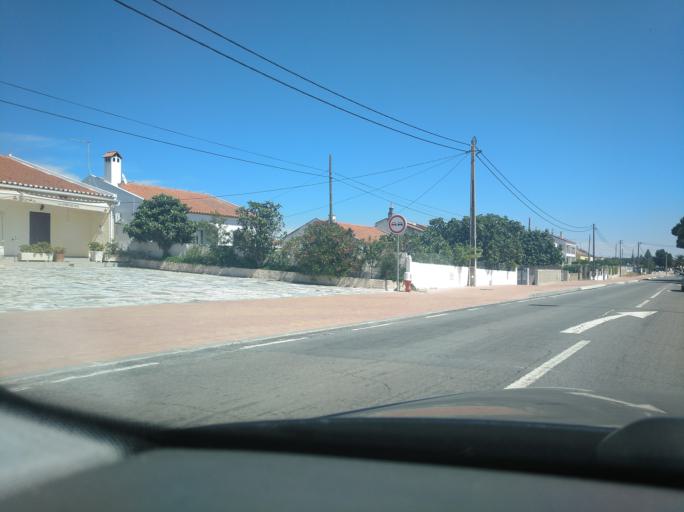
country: PT
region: Beja
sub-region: Castro Verde
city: Castro Verde
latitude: 37.6111
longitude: -8.0820
